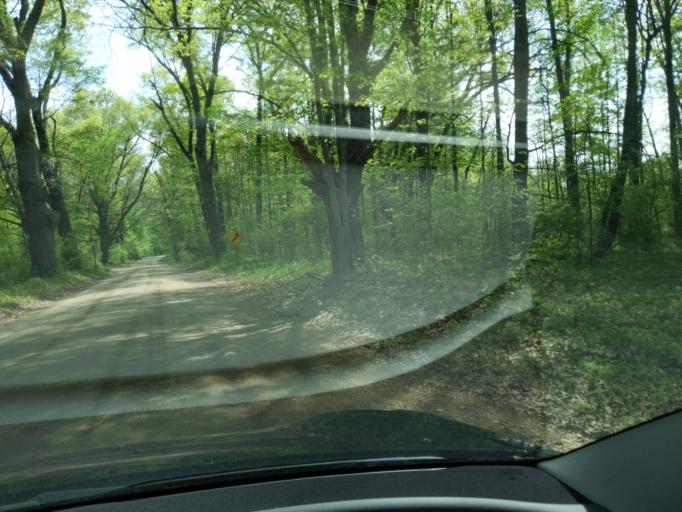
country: US
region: Michigan
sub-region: Ingham County
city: Stockbridge
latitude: 42.4385
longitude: -84.0749
